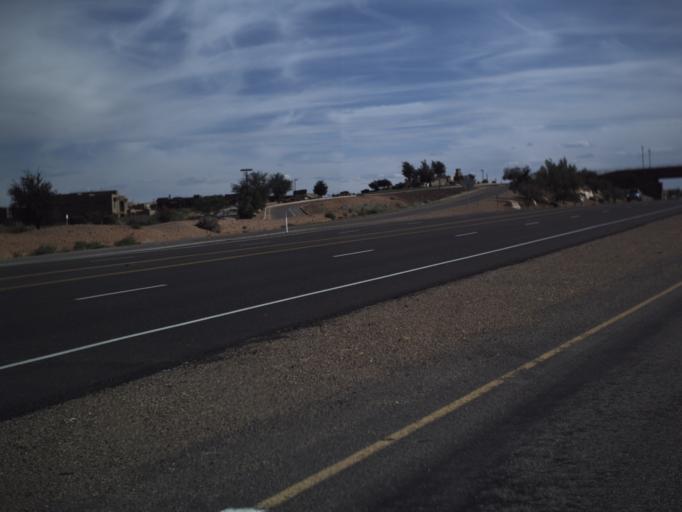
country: US
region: Utah
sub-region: Washington County
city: Ivins
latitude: 37.1974
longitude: -113.6241
